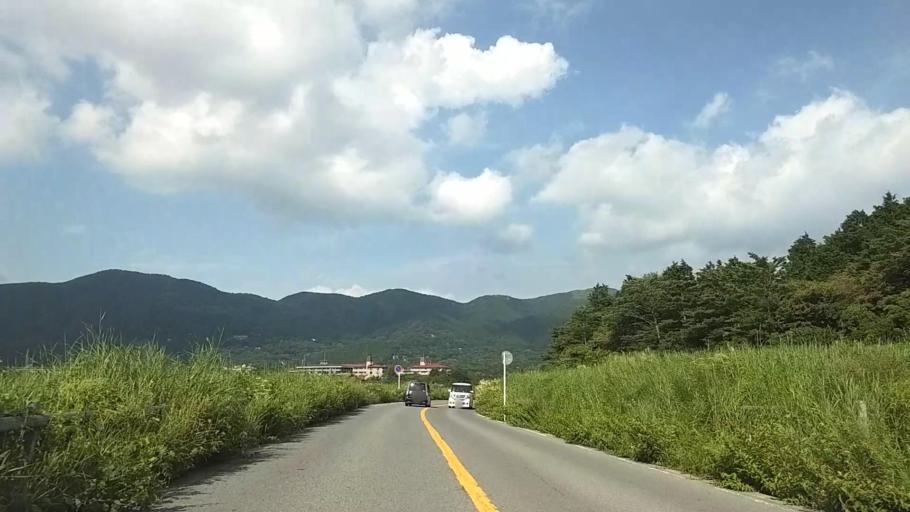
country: JP
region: Shizuoka
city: Gotemba
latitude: 35.2627
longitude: 139.0064
